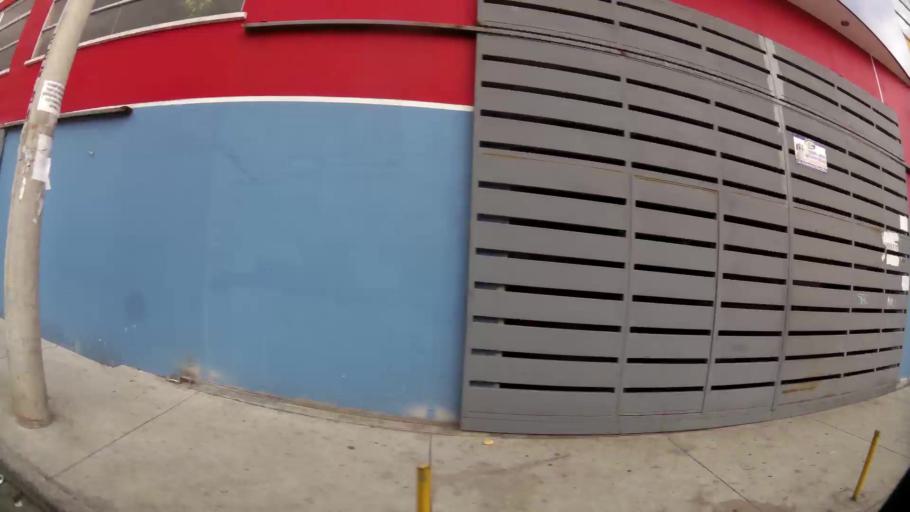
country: EC
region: Pichincha
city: Quito
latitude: -0.2783
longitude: -78.5342
